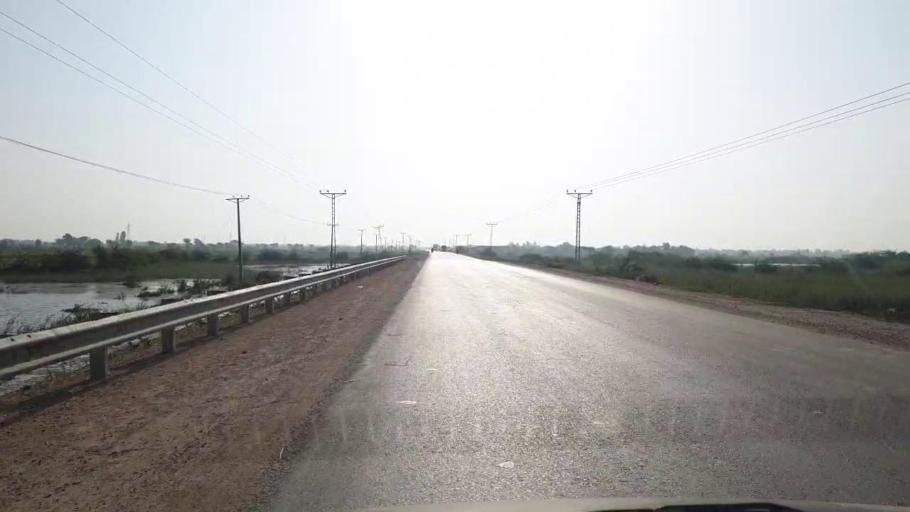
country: PK
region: Sindh
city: Badin
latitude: 24.6743
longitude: 68.8526
